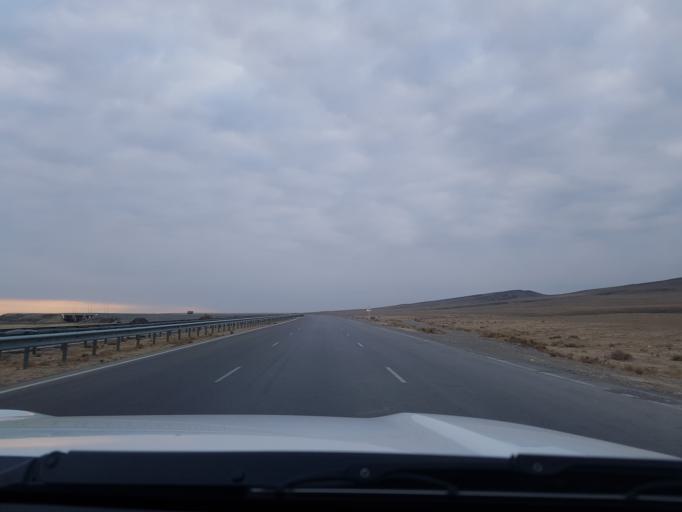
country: IR
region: Razavi Khorasan
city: Dargaz
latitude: 37.6839
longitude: 59.0708
